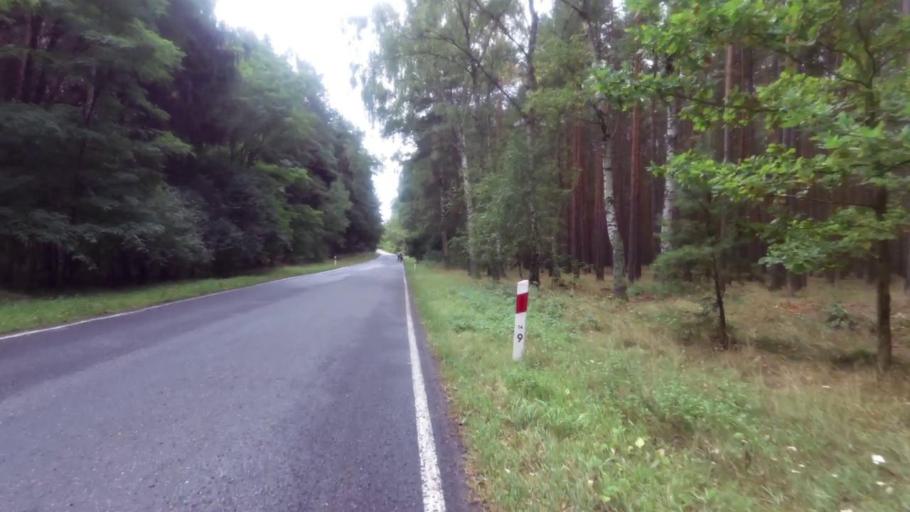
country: PL
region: West Pomeranian Voivodeship
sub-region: Powiat mysliborski
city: Debno
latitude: 52.7009
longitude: 14.6457
